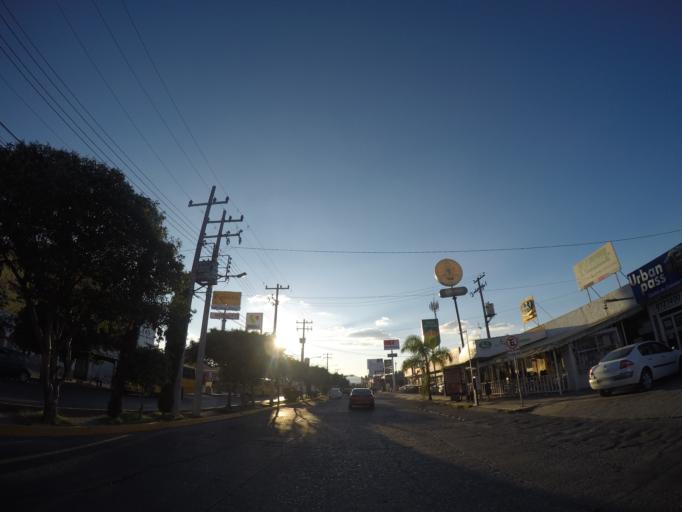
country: MX
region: San Luis Potosi
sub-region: San Luis Potosi
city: San Luis Potosi
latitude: 22.1352
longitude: -100.9796
